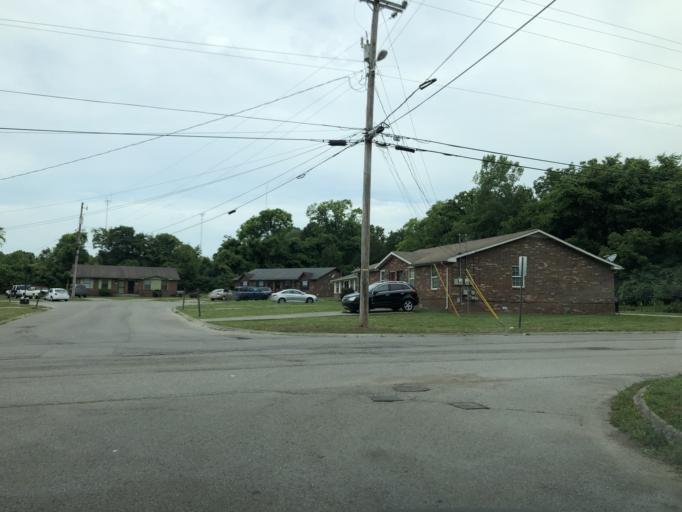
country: US
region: Tennessee
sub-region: Davidson County
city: Goodlettsville
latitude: 36.2597
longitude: -86.7658
